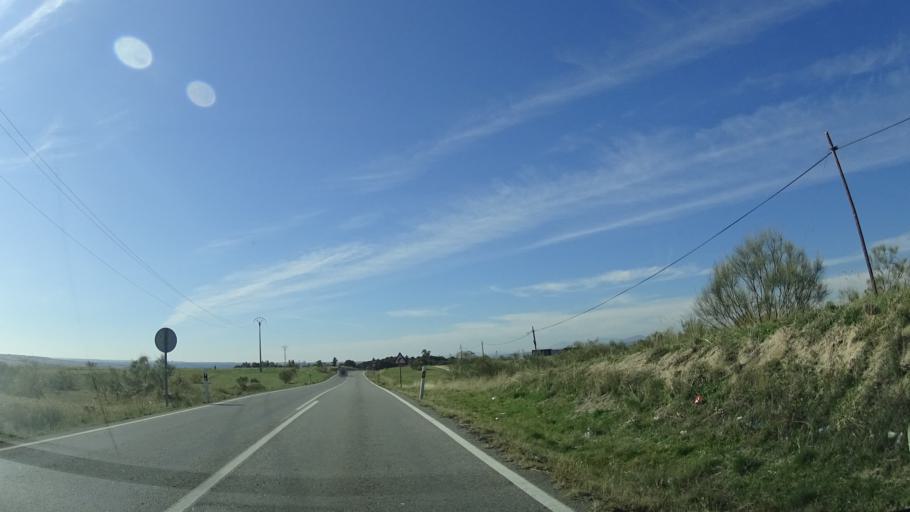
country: ES
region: Madrid
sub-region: Provincia de Madrid
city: Las Rozas de Madrid
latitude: 40.4971
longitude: -3.9027
